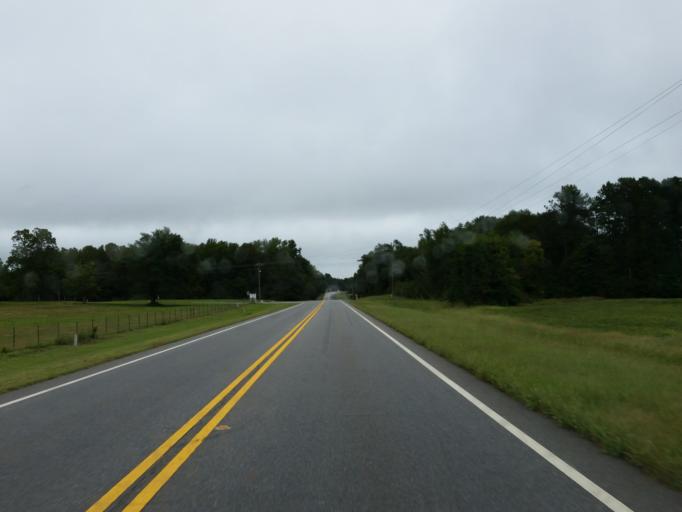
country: US
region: Georgia
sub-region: Lamar County
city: Barnesville
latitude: 33.0118
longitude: -84.1269
